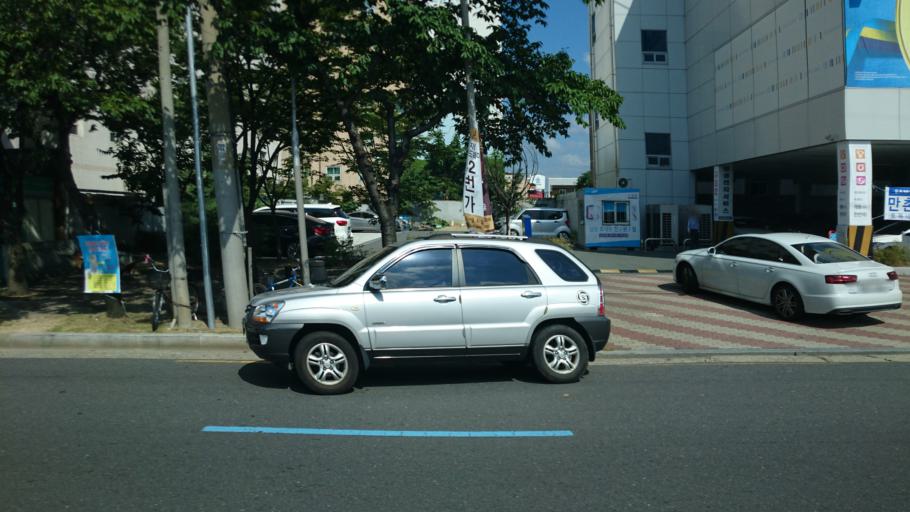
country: KR
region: Daegu
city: Daegu
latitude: 35.8765
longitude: 128.6446
